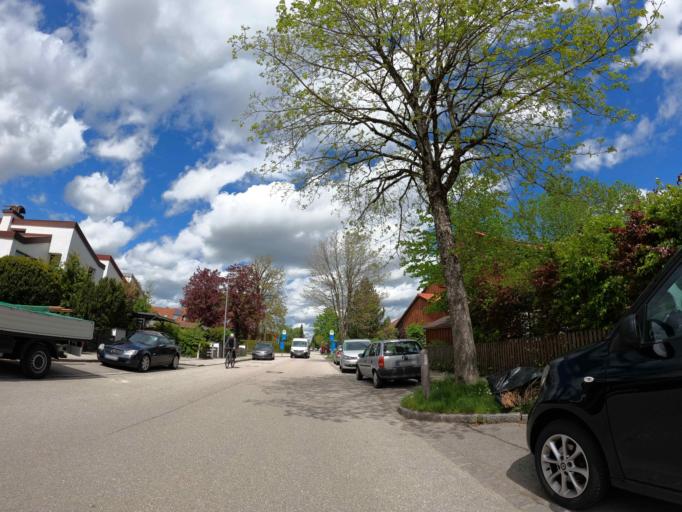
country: DE
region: Bavaria
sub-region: Upper Bavaria
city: Putzbrunn
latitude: 48.0765
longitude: 11.7014
